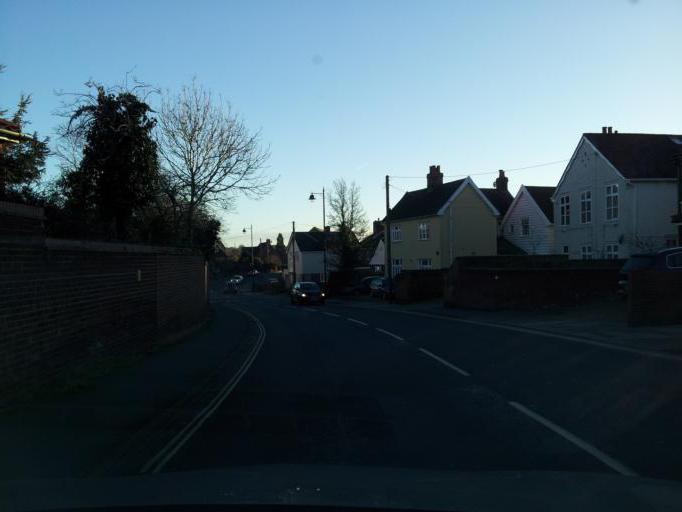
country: GB
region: England
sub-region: Suffolk
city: Woodbridge
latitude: 52.0905
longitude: 1.3132
